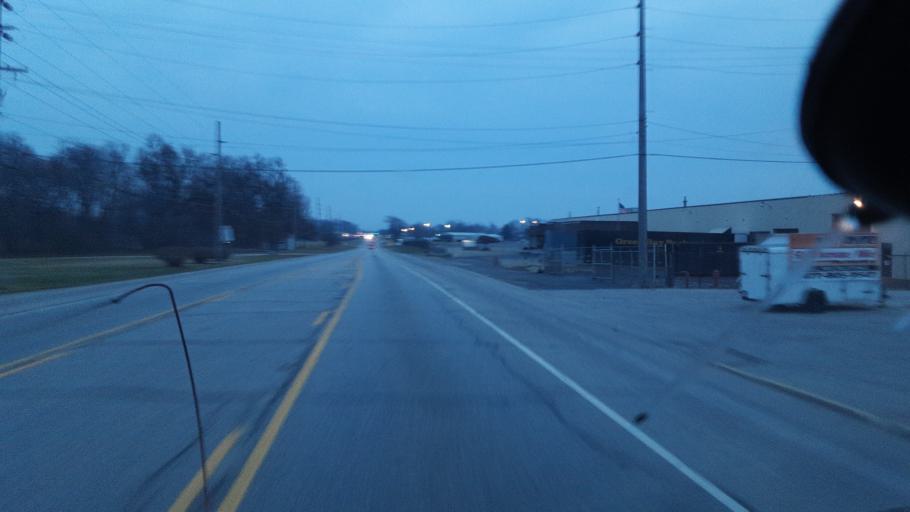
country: US
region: Indiana
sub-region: Elkhart County
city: Middlebury
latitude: 41.6626
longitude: -85.7196
